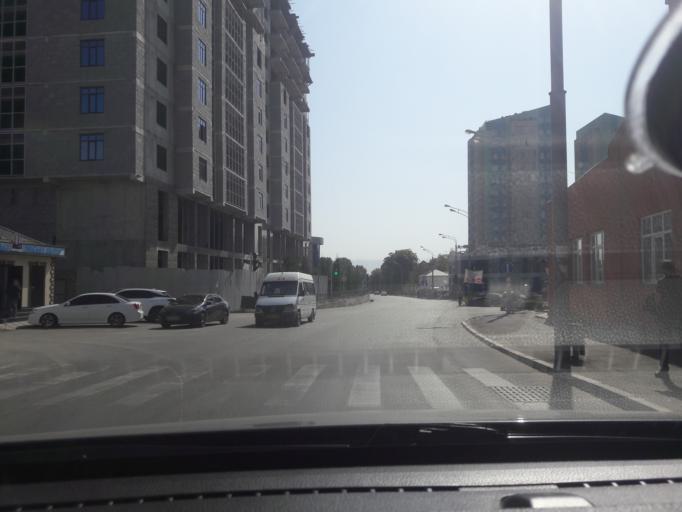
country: TJ
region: Dushanbe
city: Dushanbe
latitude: 38.5758
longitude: 68.8002
